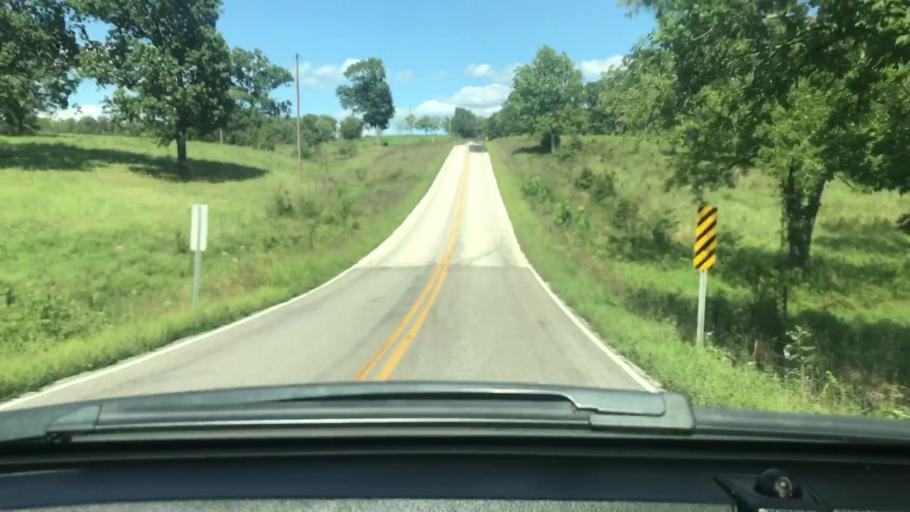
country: US
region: Missouri
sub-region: Wright County
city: Hartville
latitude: 37.3737
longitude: -92.3856
